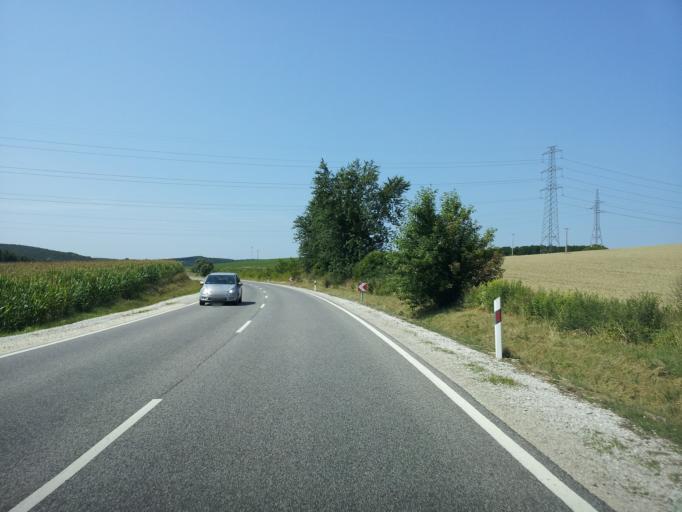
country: HU
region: Zala
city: Pacsa
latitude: 46.8310
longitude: 17.0191
